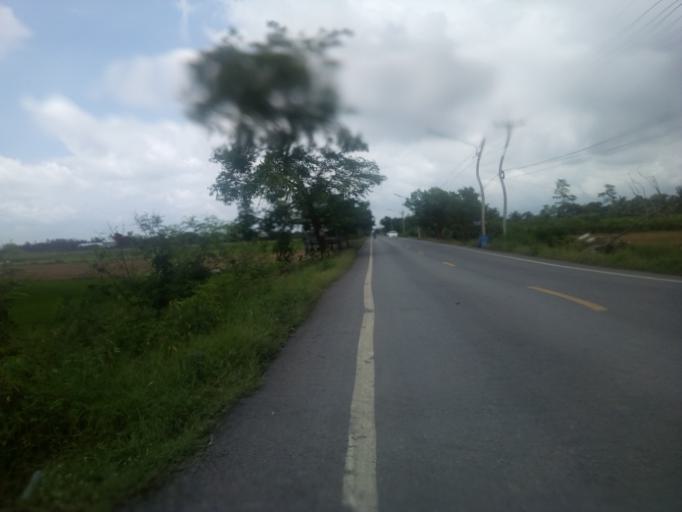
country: TH
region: Pathum Thani
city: Ban Lam Luk Ka
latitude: 14.0232
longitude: 100.8239
